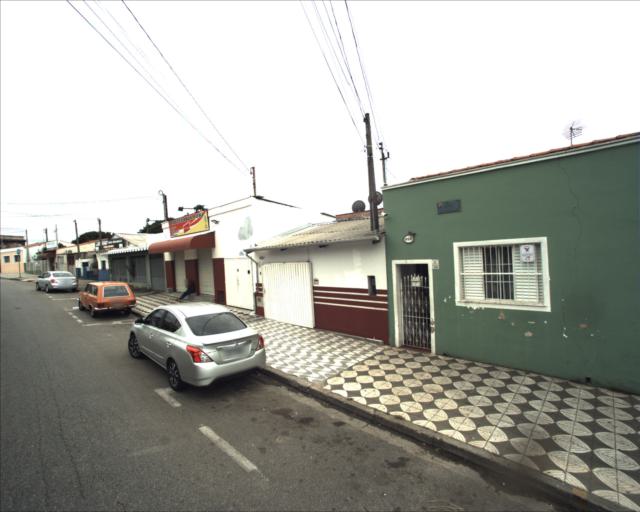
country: BR
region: Sao Paulo
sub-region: Sorocaba
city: Sorocaba
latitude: -23.5193
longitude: -47.4431
